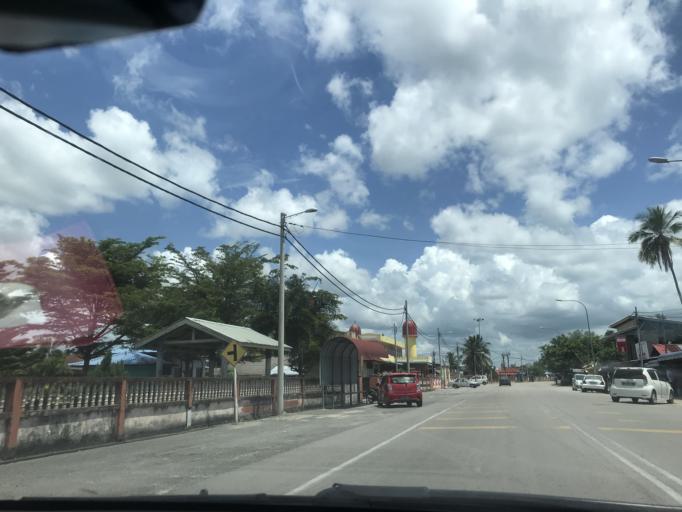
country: TH
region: Narathiwat
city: Tak Bai
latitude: 6.2301
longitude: 102.0961
